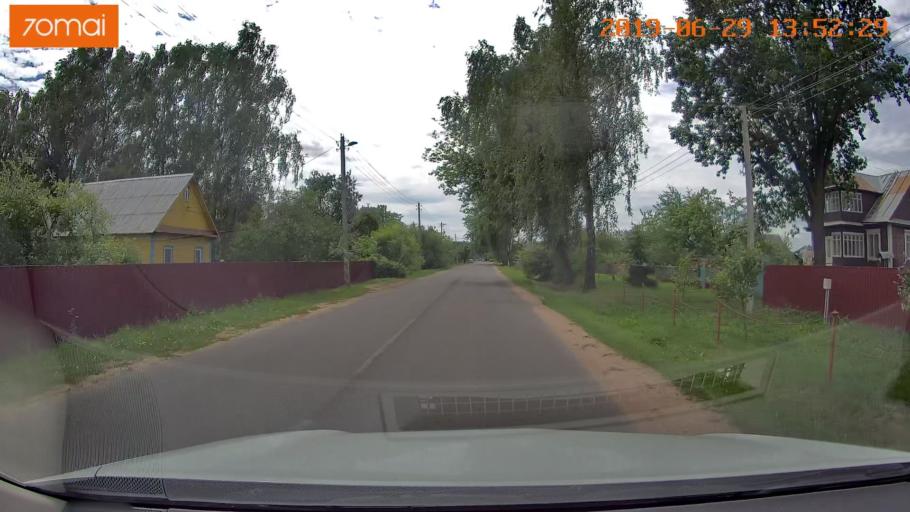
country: BY
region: Minsk
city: Slutsk
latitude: 52.9952
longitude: 27.5543
